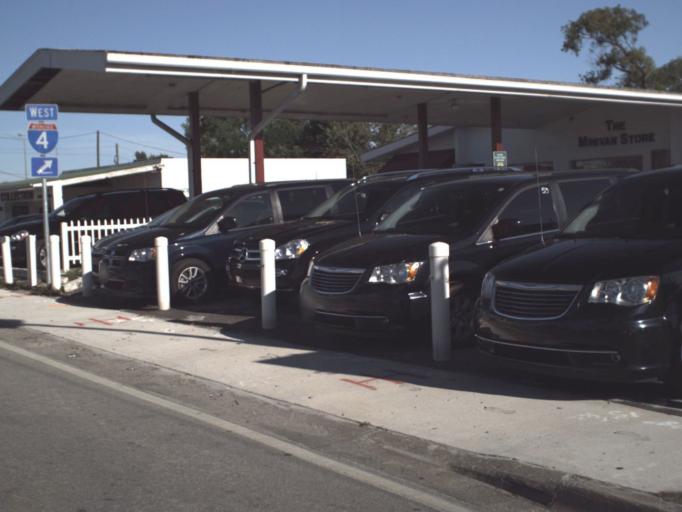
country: US
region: Florida
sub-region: Orange County
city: Fairview Shores
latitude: 28.5929
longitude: -81.3835
